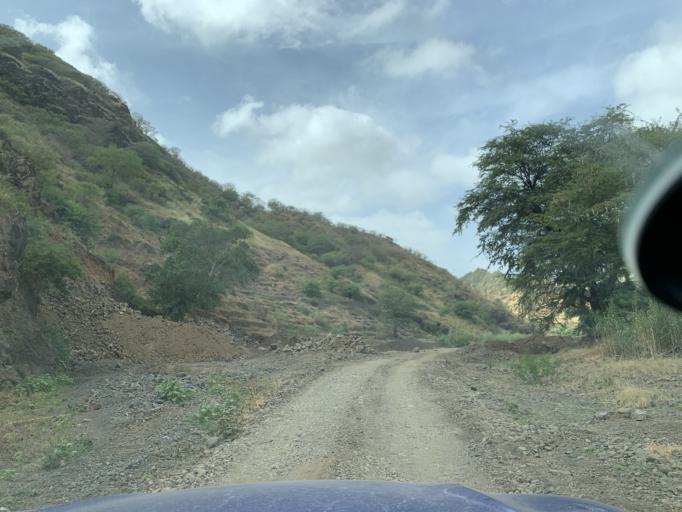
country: CV
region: Santa Cruz
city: Santa Cruz
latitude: 15.1067
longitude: -23.5806
